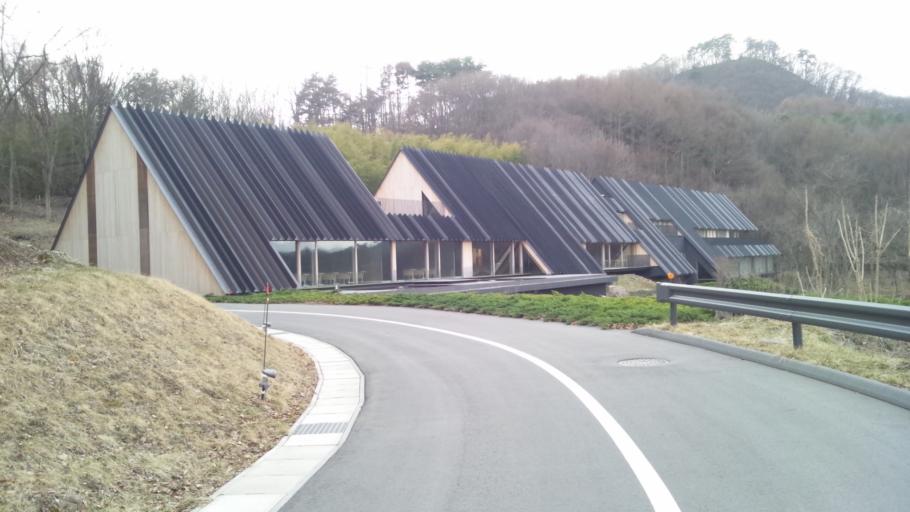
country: JP
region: Nagano
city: Komoro
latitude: 36.3240
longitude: 138.3951
